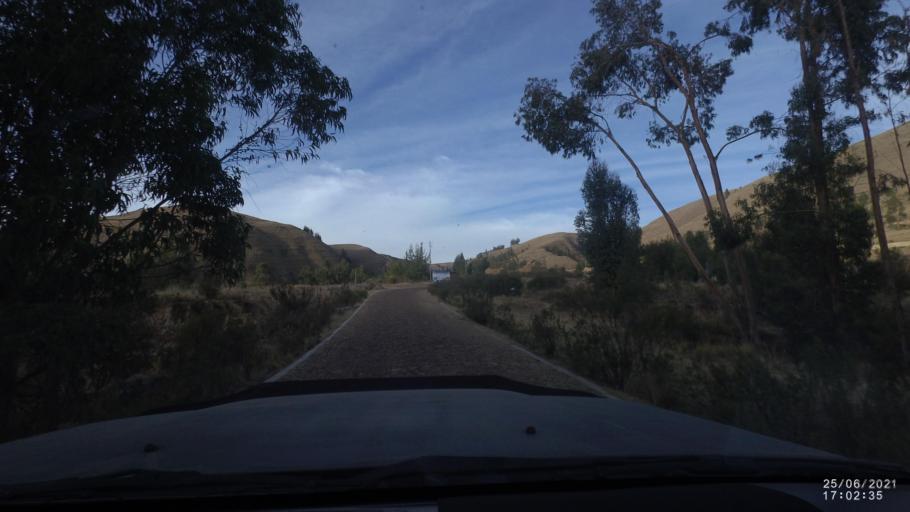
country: BO
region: Cochabamba
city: Arani
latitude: -17.8357
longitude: -65.7326
